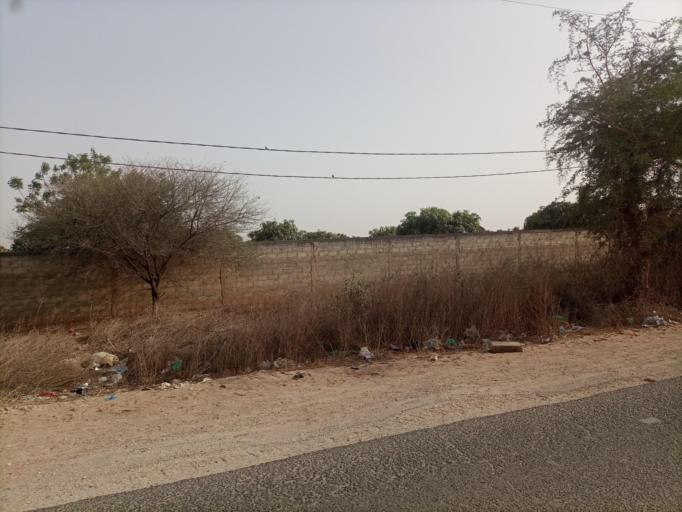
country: SN
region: Thies
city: Nguekhokh
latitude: 14.5864
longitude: -17.0259
